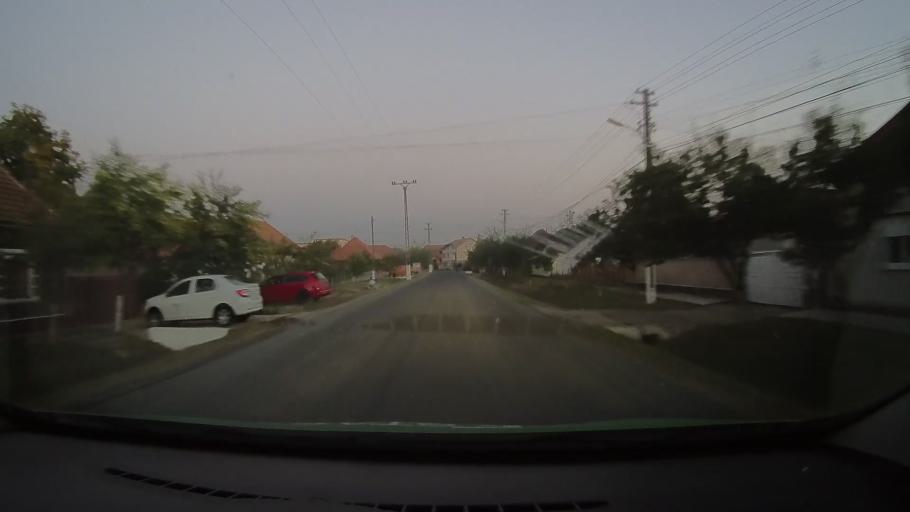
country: RO
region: Arad
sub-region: Comuna Livada
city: Livada
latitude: 46.2264
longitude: 21.3812
